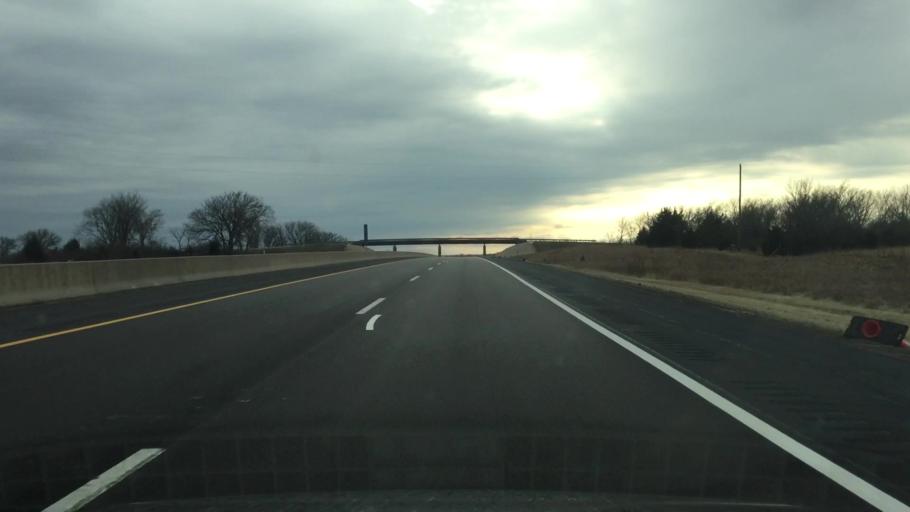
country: US
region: Kansas
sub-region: Lyon County
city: Emporia
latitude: 38.5944
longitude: -96.0754
